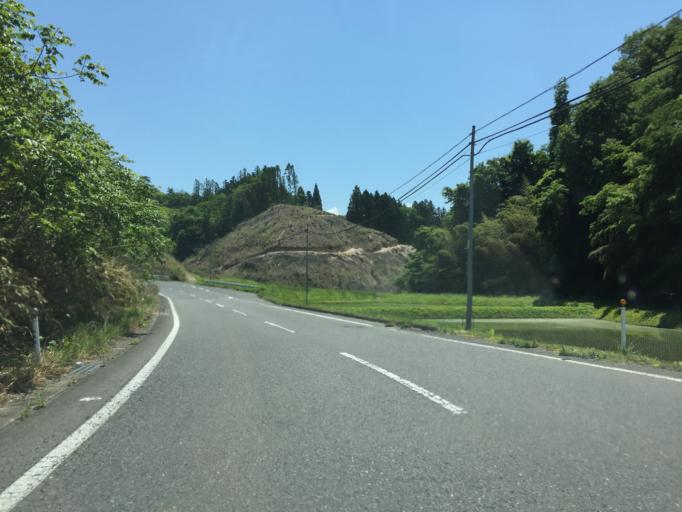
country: JP
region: Fukushima
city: Miharu
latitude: 37.4897
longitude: 140.5157
